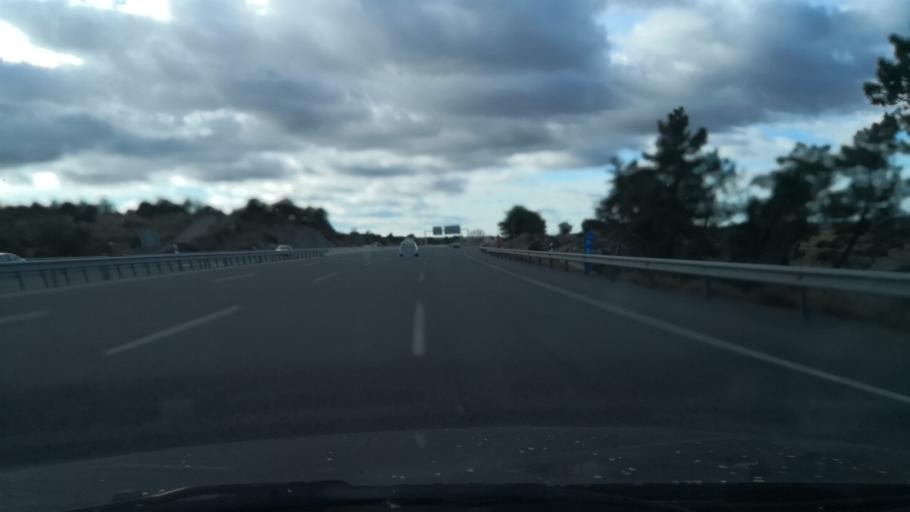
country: ES
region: Castille and Leon
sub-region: Provincia de Segovia
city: Villacastin
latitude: 40.7709
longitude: -4.4034
